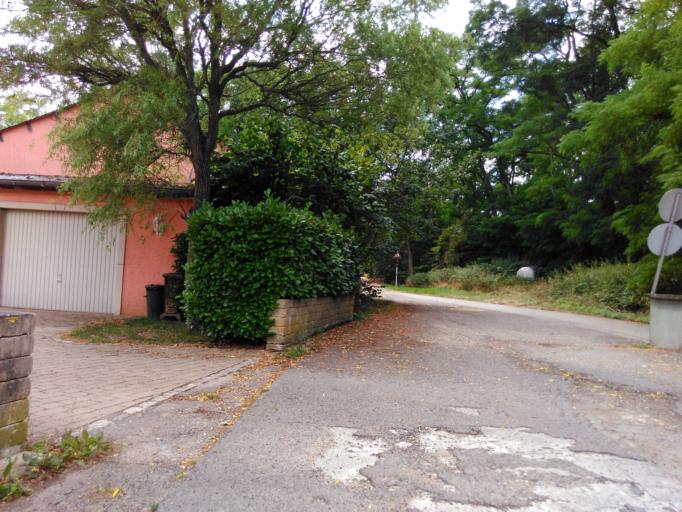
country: LU
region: Grevenmacher
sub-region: Canton de Grevenmacher
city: Junglinster
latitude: 49.7319
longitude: 6.3011
